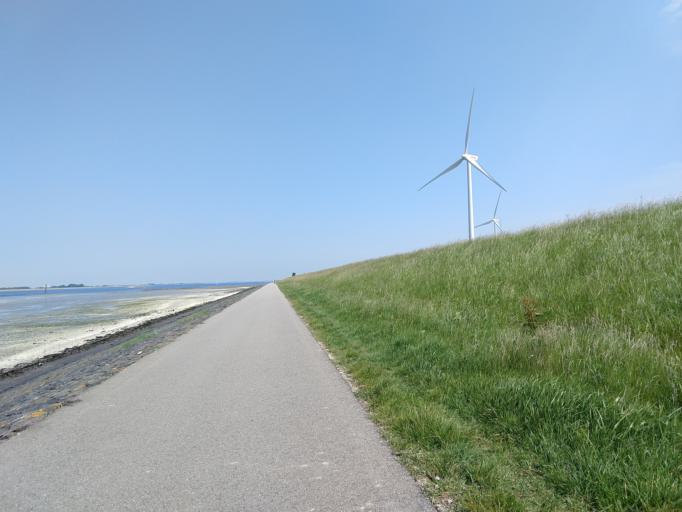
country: NL
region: Zeeland
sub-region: Schouwen-Duiveland
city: Bruinisse
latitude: 51.6060
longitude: 4.0493
